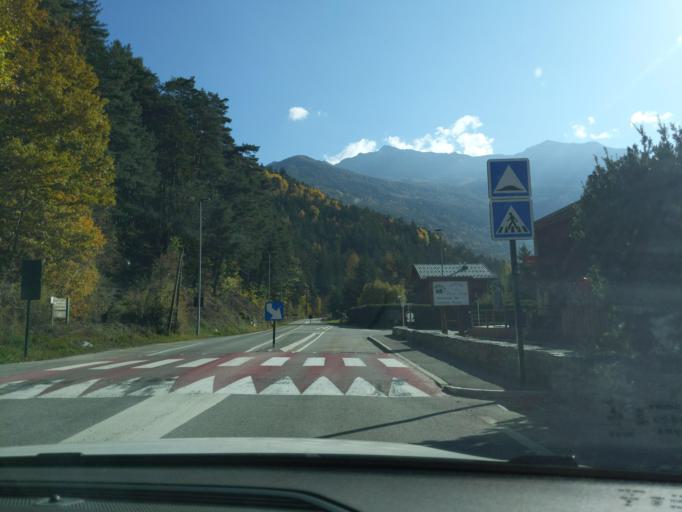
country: FR
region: Rhone-Alpes
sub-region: Departement de la Savoie
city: Seez
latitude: 45.6033
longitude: 6.8619
